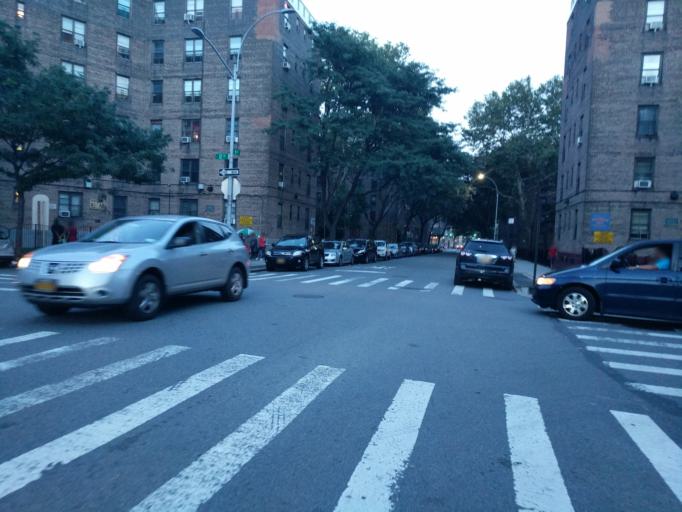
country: US
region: New York
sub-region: Queens County
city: Long Island City
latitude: 40.7549
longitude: -73.9442
